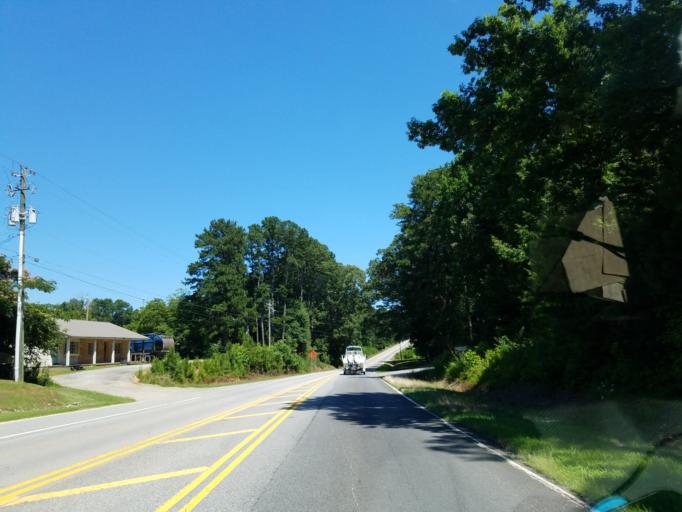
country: US
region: Georgia
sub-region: Forsyth County
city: Cumming
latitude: 34.2618
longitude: -84.0818
